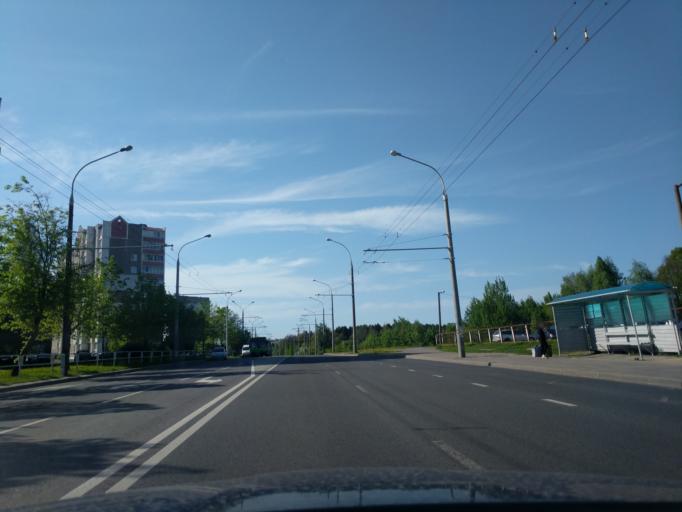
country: BY
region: Minsk
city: Novoye Medvezhino
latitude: 53.8895
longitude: 27.4416
